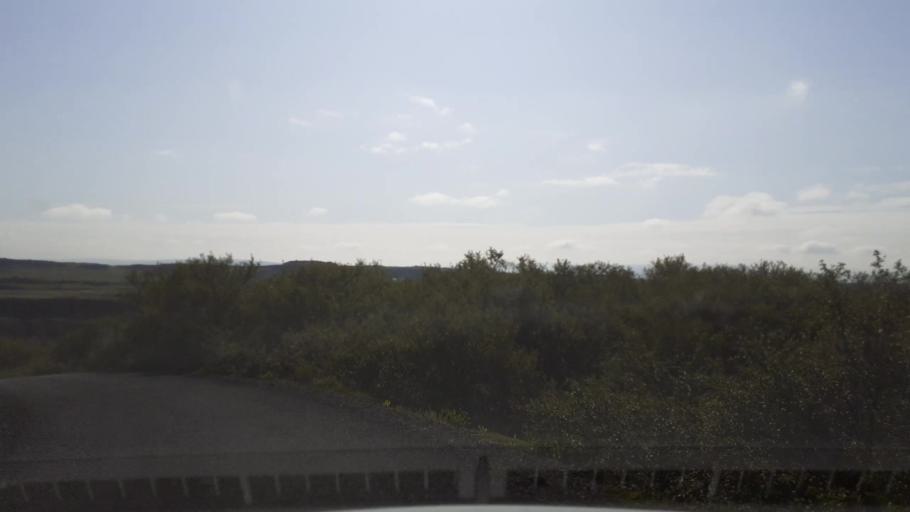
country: IS
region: West
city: Borgarnes
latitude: 64.7009
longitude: -21.6185
